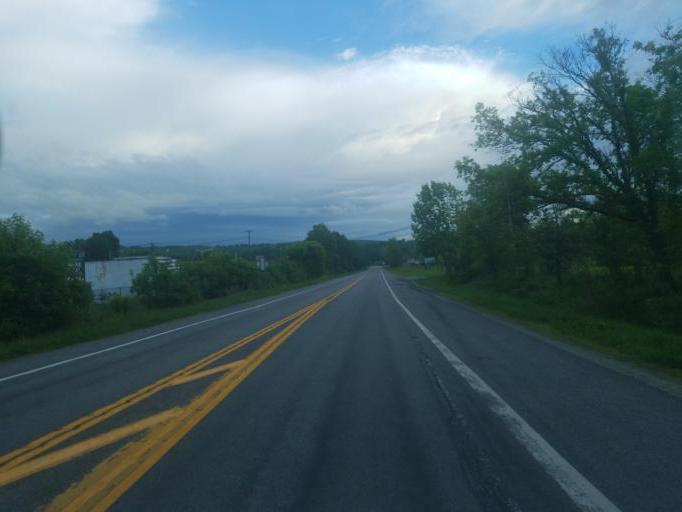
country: US
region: New York
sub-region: Herkimer County
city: Herkimer
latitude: 43.0318
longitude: -74.9834
